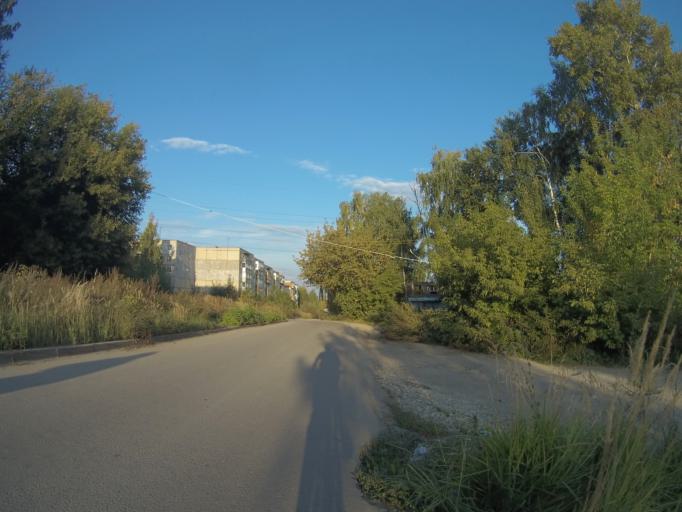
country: RU
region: Vladimir
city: Vladimir
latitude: 56.1021
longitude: 40.3498
